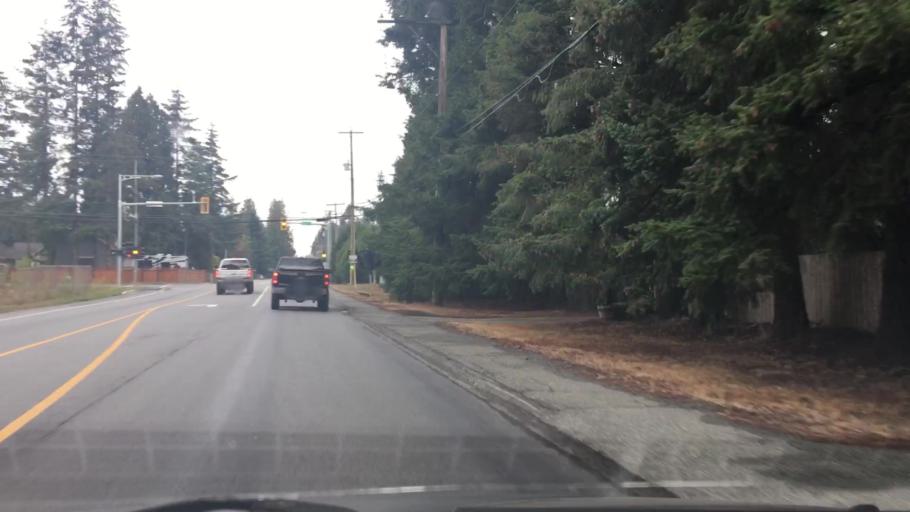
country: CA
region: British Columbia
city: Langley
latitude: 49.1040
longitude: -122.5360
